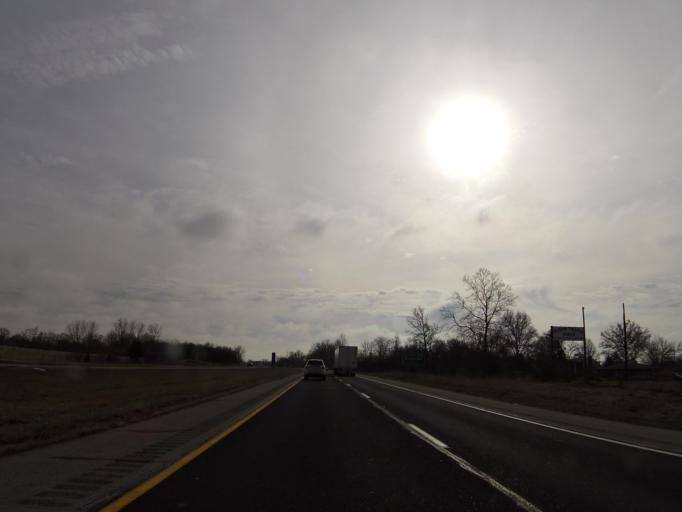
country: US
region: Indiana
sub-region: Marion County
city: Cumberland
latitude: 39.6947
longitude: -85.9892
